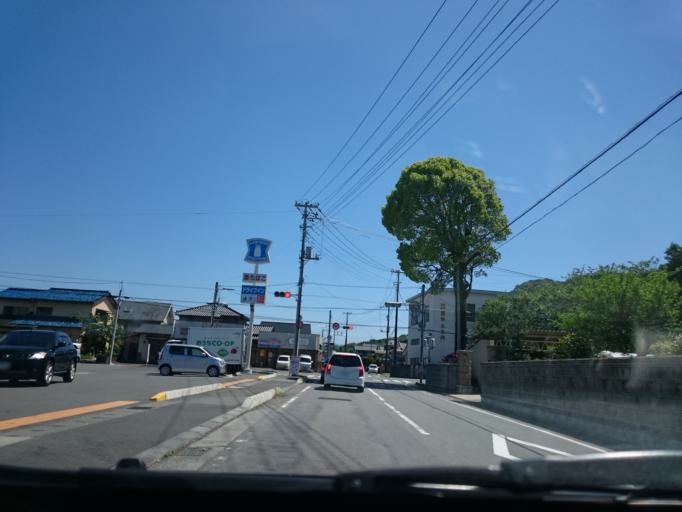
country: JP
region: Shizuoka
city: Mishima
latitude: 35.0560
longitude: 138.9321
